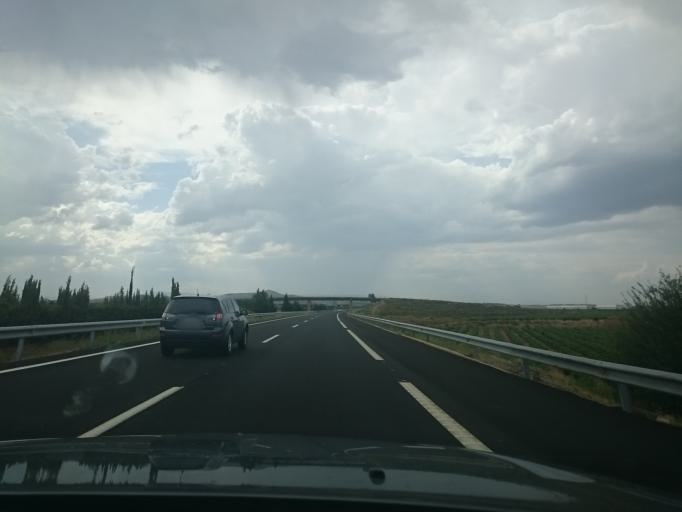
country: ES
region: La Rioja
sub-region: Provincia de La Rioja
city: Aldeanueva de Ebro
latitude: 42.2126
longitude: -1.8810
